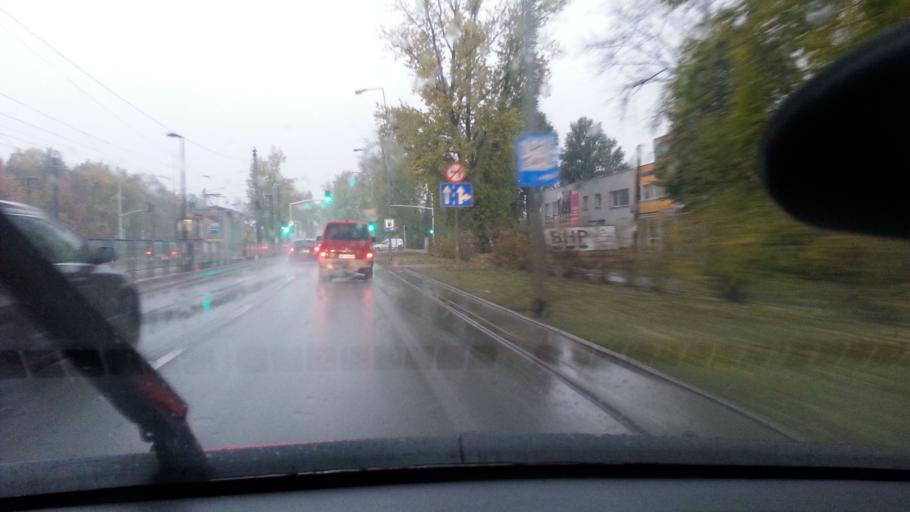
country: PL
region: Masovian Voivodeship
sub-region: Warszawa
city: Praga Polnoc
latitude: 52.2741
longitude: 21.0312
